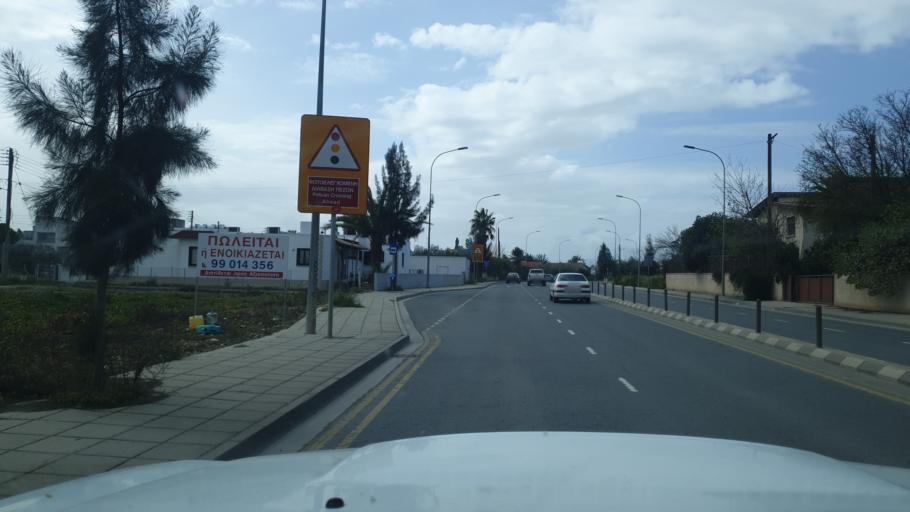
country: CY
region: Lefkosia
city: Kato Deftera
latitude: 35.1105
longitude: 33.3040
